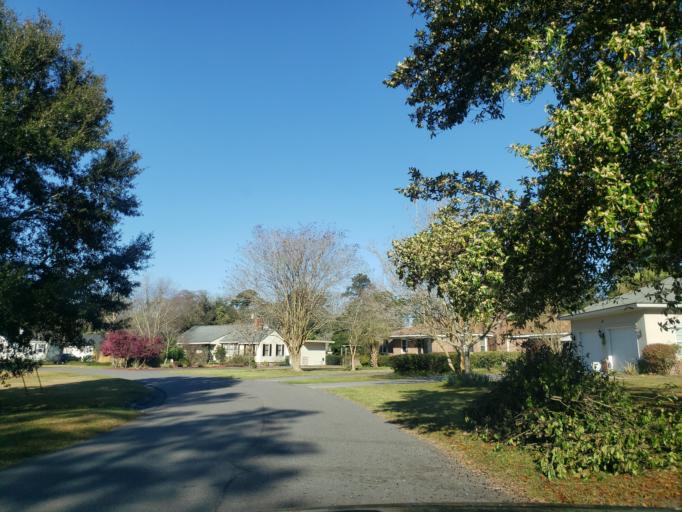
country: US
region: Georgia
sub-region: Chatham County
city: Thunderbolt
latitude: 32.0227
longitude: -81.0921
